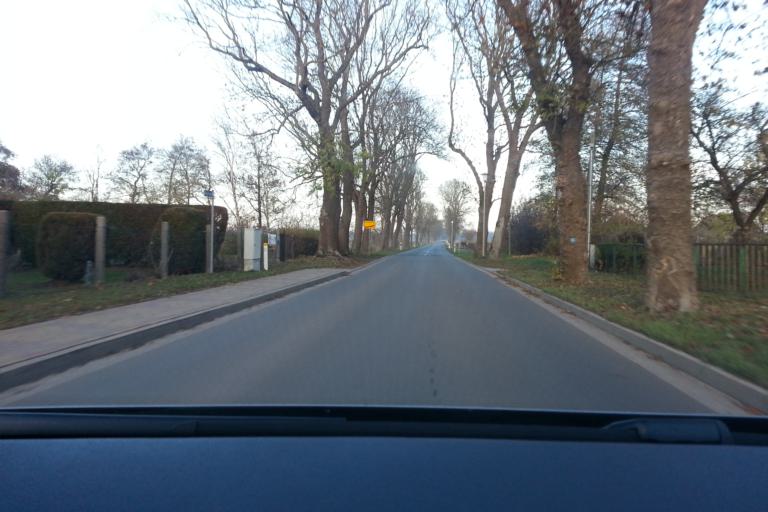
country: DE
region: Mecklenburg-Vorpommern
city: Ferdinandshof
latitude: 53.6449
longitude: 13.8617
